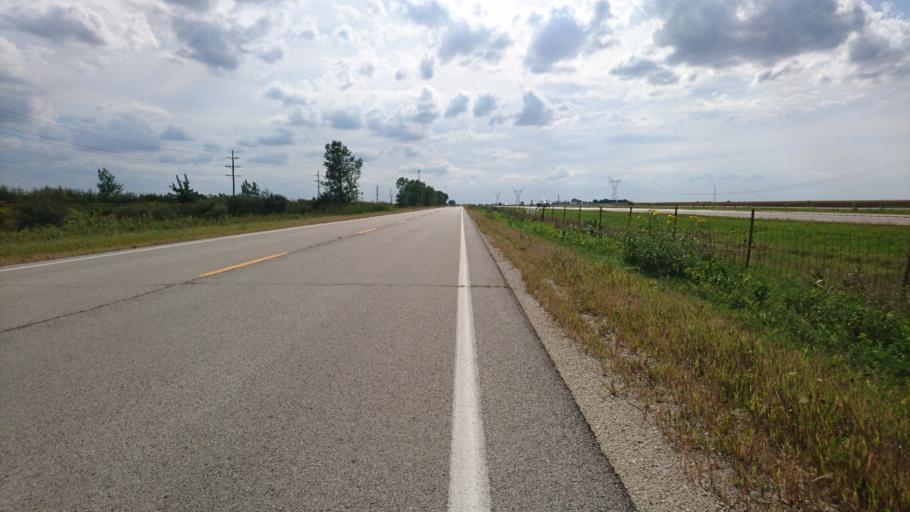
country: US
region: Illinois
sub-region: Grundy County
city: Gardner
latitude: 41.1469
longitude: -88.3601
